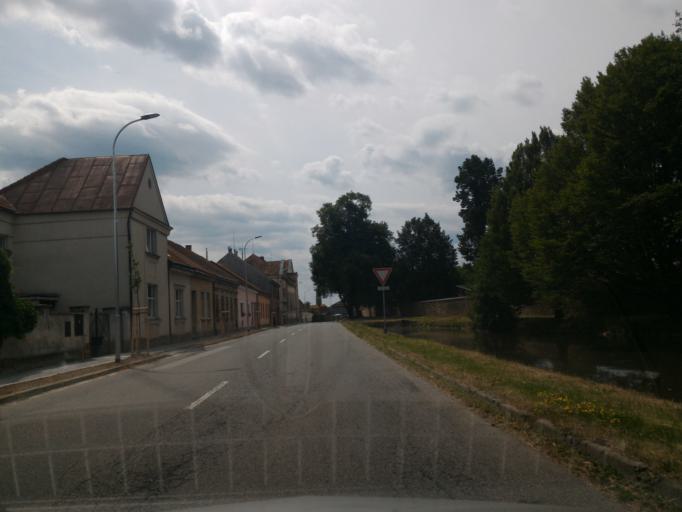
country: CZ
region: Vysocina
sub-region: Okres Jihlava
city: Telc
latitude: 49.1890
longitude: 15.4513
